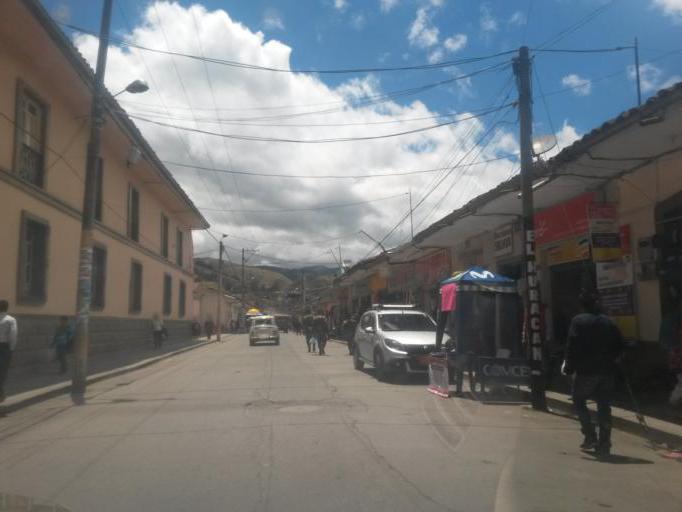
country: CO
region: Cauca
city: Silvia
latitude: 2.6115
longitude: -76.3783
